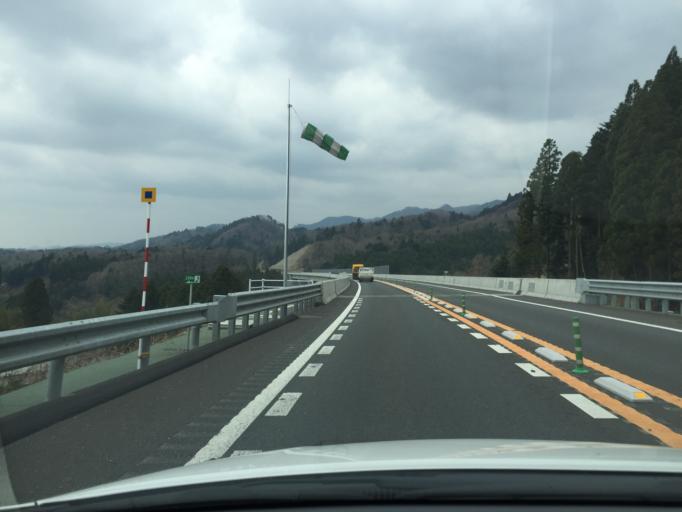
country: JP
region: Miyagi
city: Marumori
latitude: 37.8270
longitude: 140.8754
